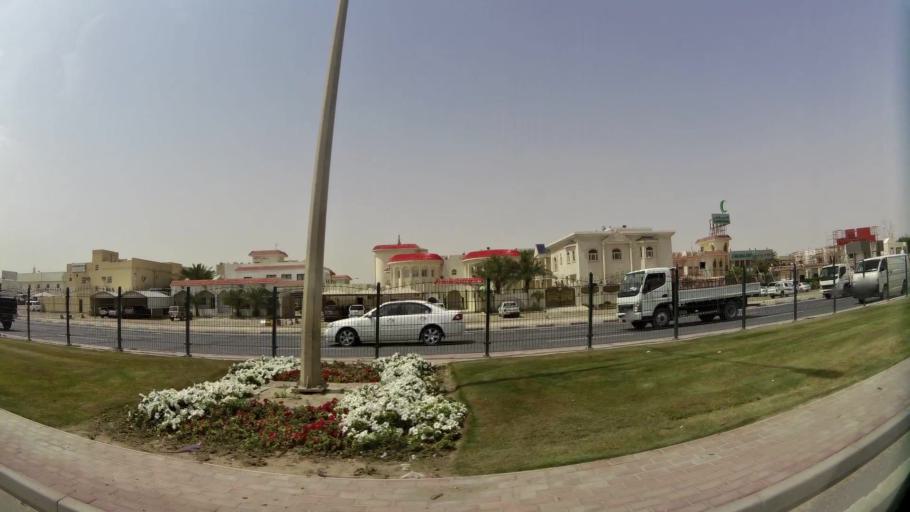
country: QA
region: Baladiyat ar Rayyan
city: Ar Rayyan
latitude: 25.2415
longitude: 51.4314
